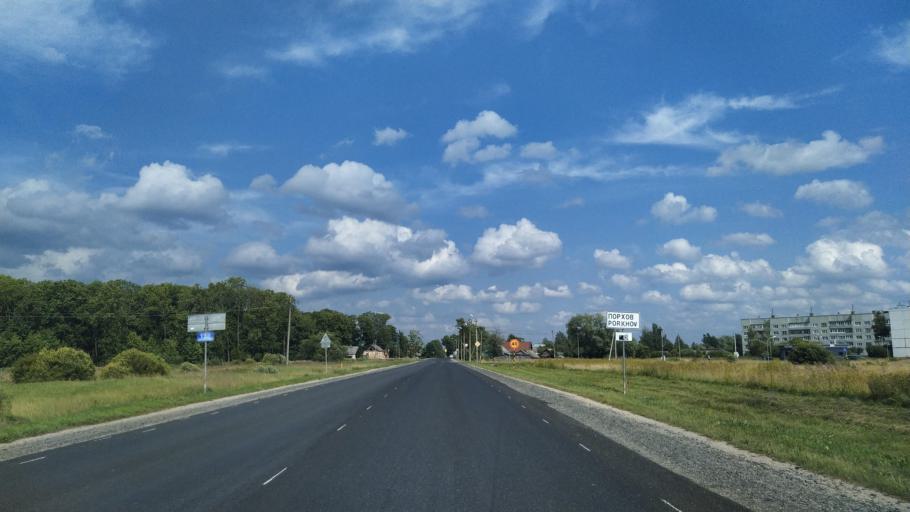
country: RU
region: Pskov
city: Porkhov
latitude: 57.7593
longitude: 29.5402
